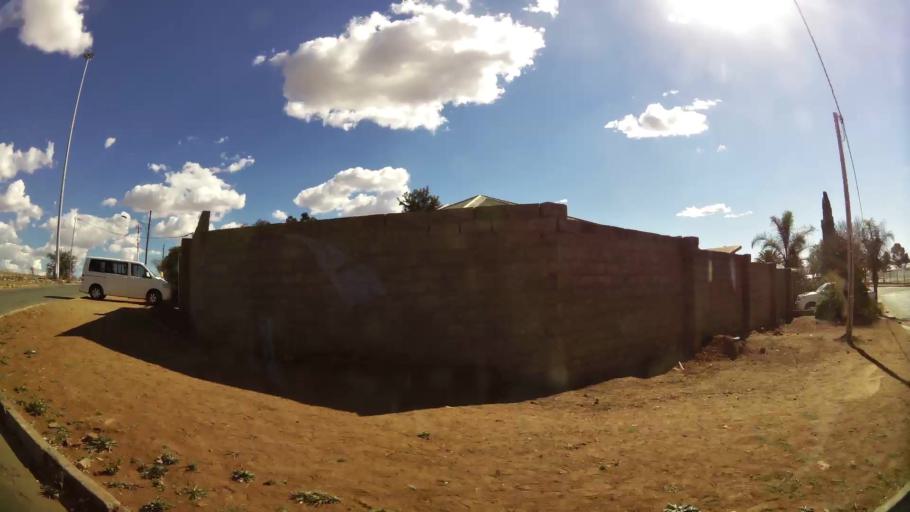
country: ZA
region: North-West
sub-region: Dr Kenneth Kaunda District Municipality
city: Klerksdorp
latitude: -26.8740
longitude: 26.5957
